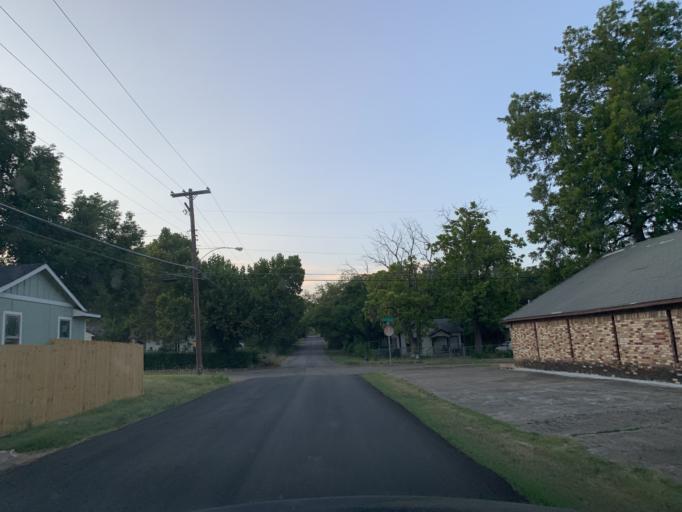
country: US
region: Texas
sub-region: Dallas County
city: Dallas
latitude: 32.6989
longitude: -96.8025
